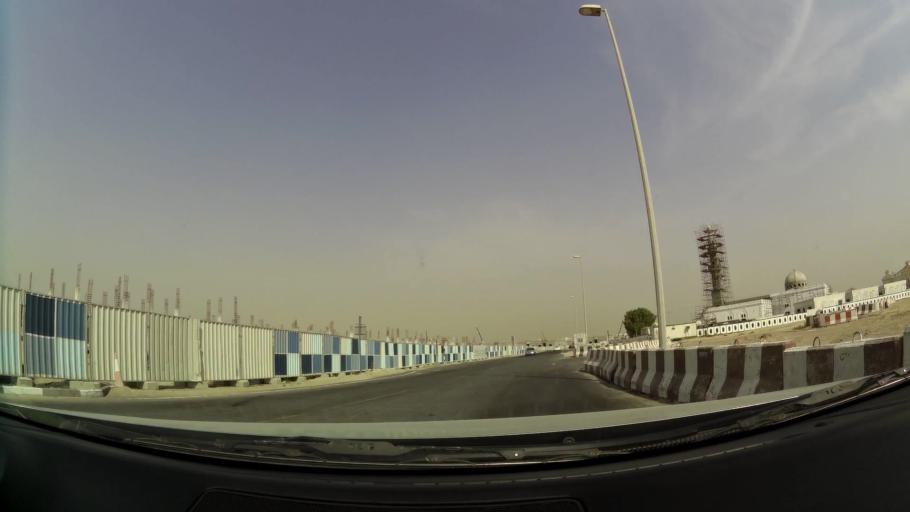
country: AE
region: Ash Shariqah
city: Sharjah
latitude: 25.2639
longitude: 55.4411
